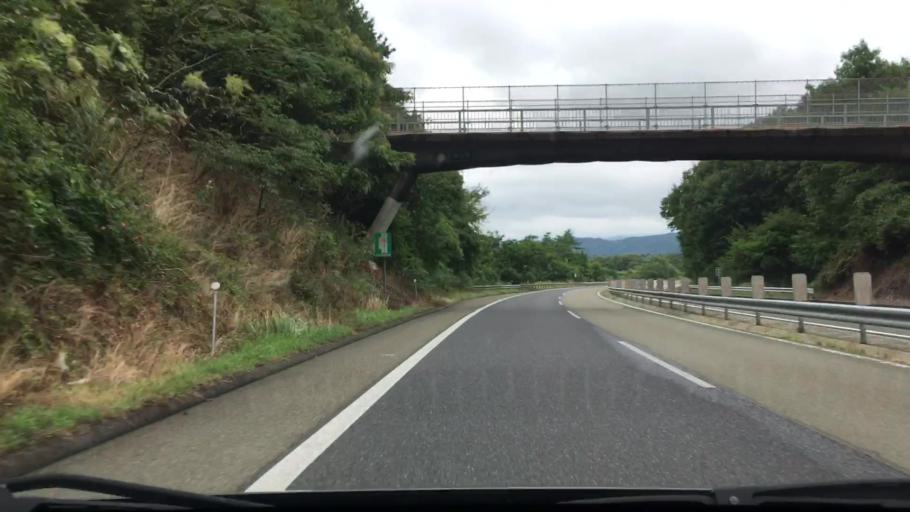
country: JP
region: Hiroshima
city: Shobara
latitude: 34.8307
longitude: 133.0473
